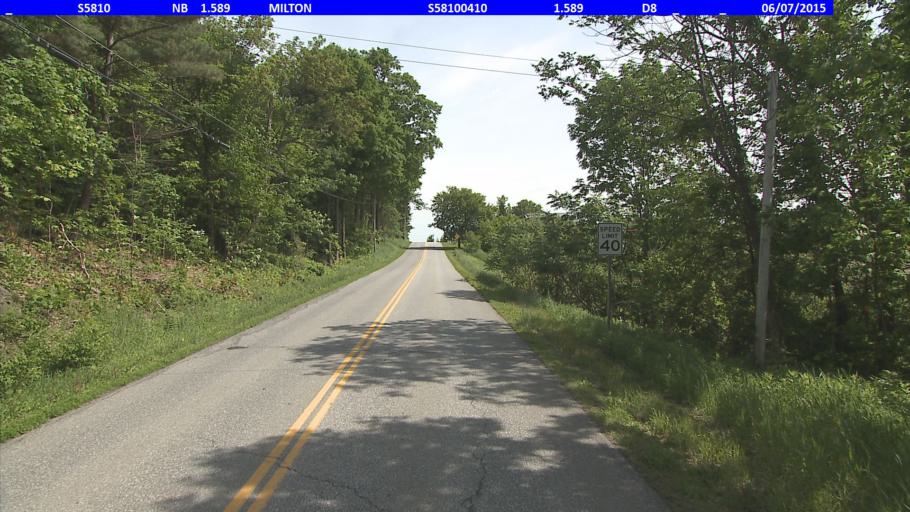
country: US
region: Vermont
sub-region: Chittenden County
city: Milton
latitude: 44.6040
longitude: -73.1255
